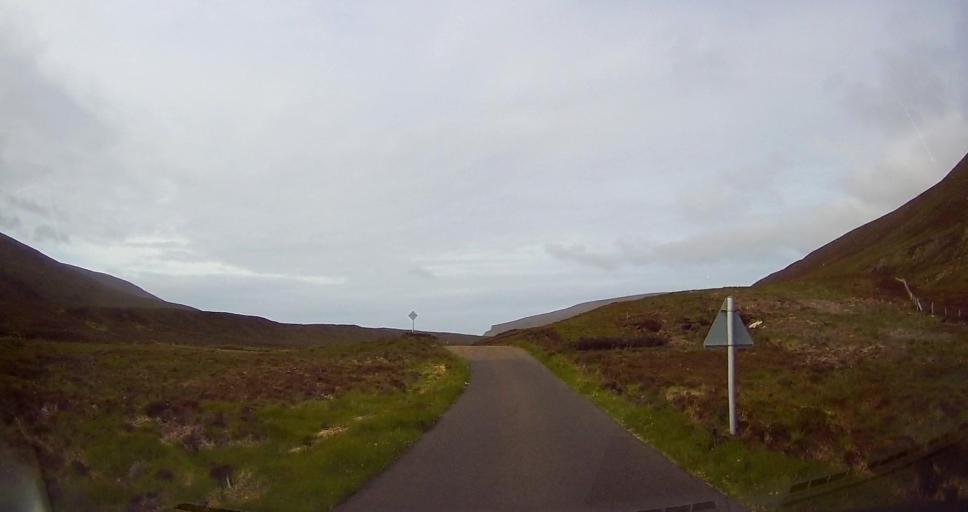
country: GB
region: Scotland
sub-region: Orkney Islands
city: Stromness
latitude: 58.8827
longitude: -3.3407
